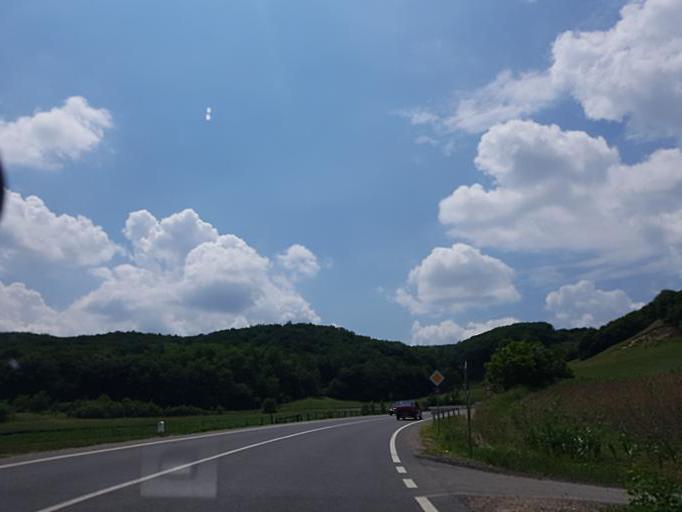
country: RO
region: Sibiu
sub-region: Comuna Slimnic
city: Slimnic
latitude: 45.9524
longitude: 24.1709
